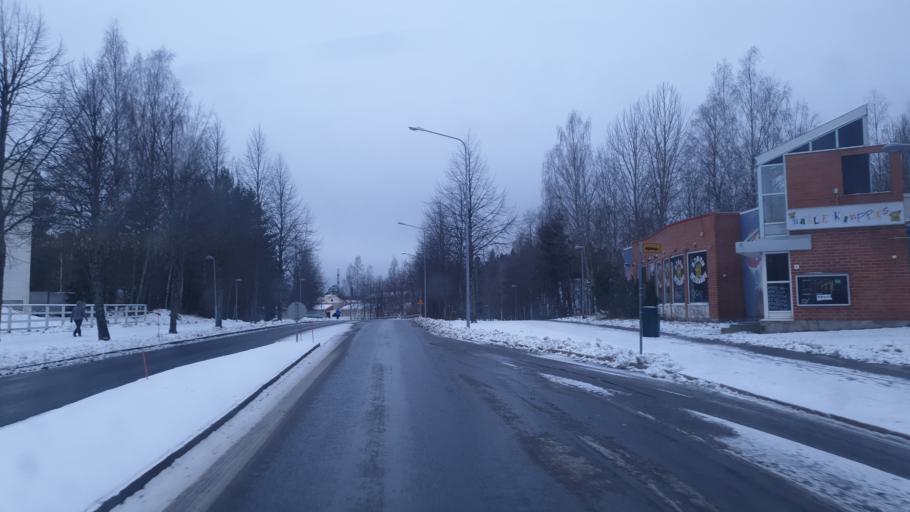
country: FI
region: Northern Savo
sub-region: Kuopio
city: Kuopio
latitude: 62.8356
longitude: 27.6238
